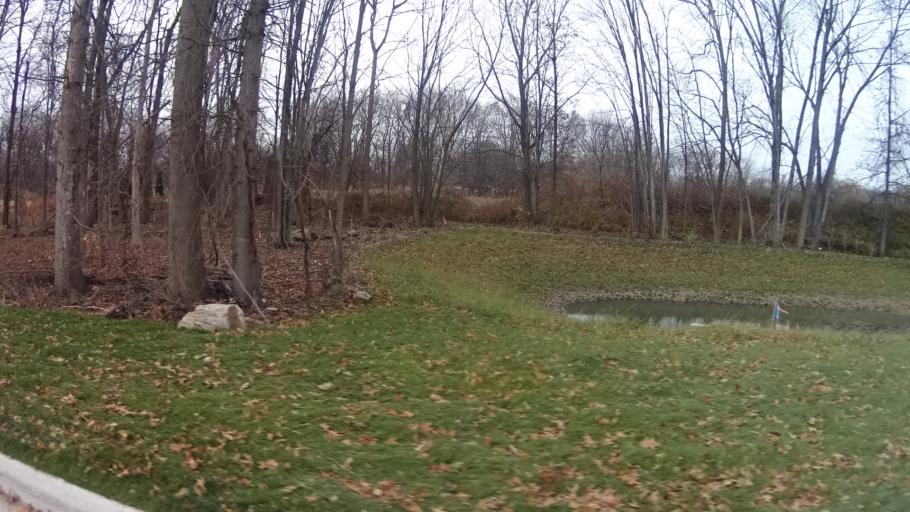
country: US
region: Ohio
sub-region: Lorain County
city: North Ridgeville
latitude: 41.3910
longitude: -82.0055
